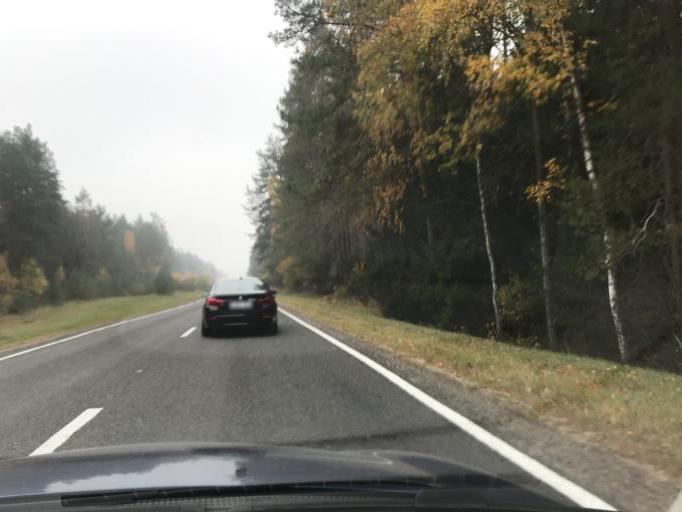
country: LT
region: Alytaus apskritis
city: Druskininkai
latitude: 53.8847
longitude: 23.9066
